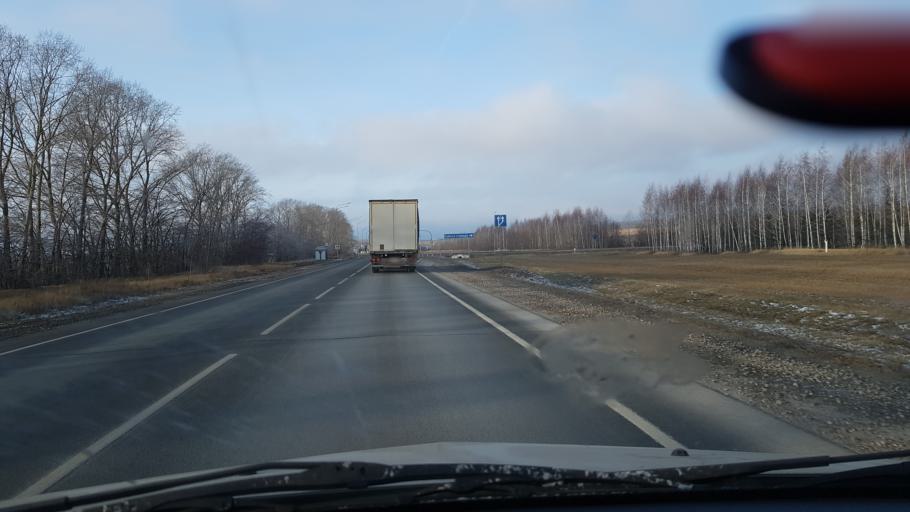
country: RU
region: Tatarstan
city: Laishevo
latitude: 55.3902
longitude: 49.8149
